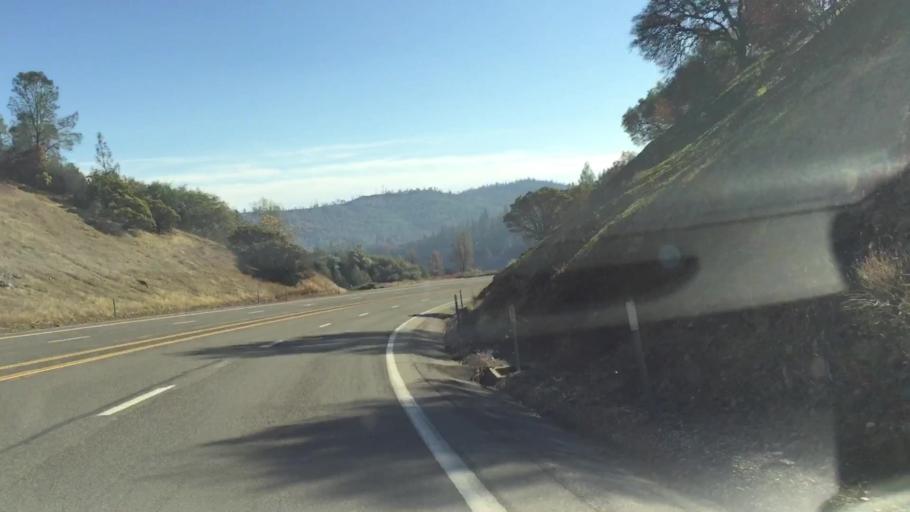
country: US
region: California
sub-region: Butte County
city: Berry Creek
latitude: 39.6717
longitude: -121.5266
